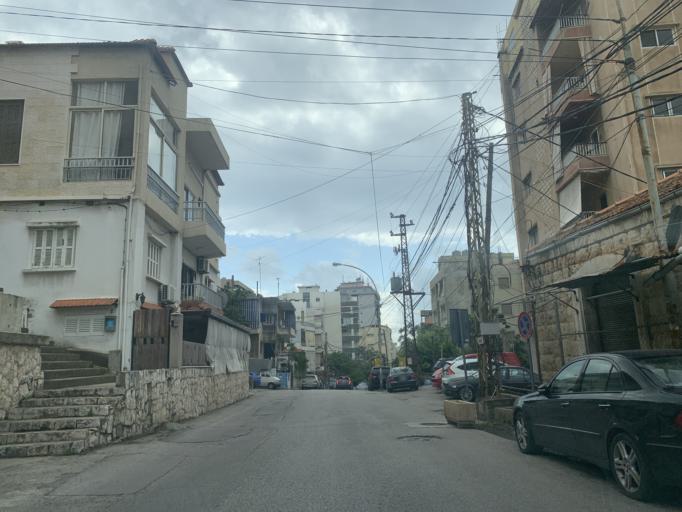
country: LB
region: Mont-Liban
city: Djounie
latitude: 33.9848
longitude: 35.6417
